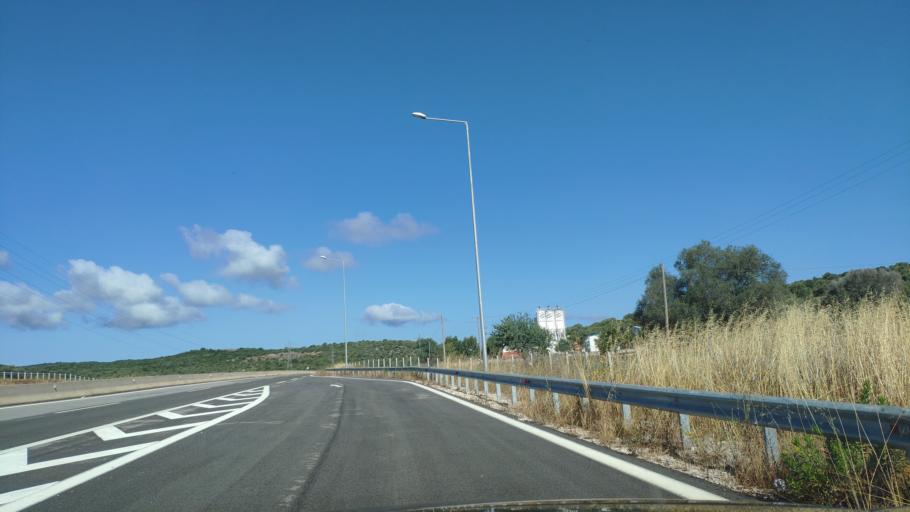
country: GR
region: West Greece
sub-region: Nomos Aitolias kai Akarnanias
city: Vonitsa
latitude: 38.9035
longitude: 20.8590
